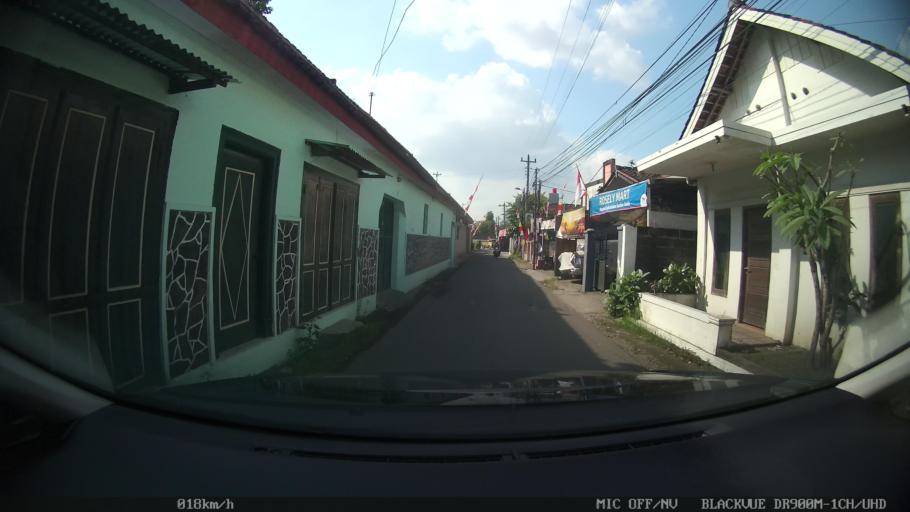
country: ID
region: Daerah Istimewa Yogyakarta
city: Sewon
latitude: -7.8333
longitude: 110.4019
